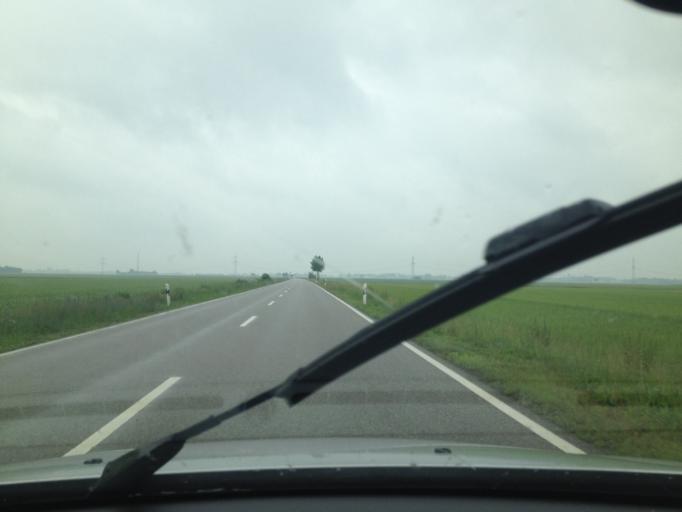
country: DE
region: Bavaria
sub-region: Swabia
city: Untermeitingen
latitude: 48.1739
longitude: 10.8037
